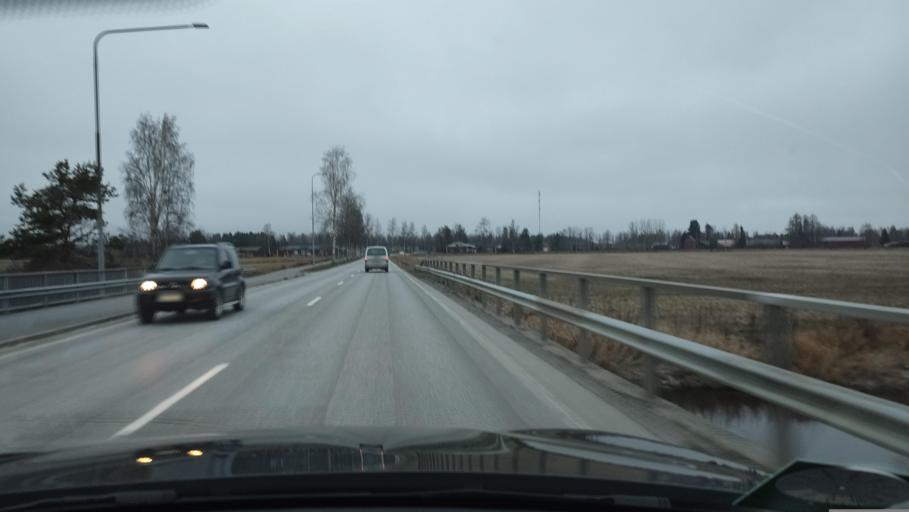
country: FI
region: Southern Ostrobothnia
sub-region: Suupohja
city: Kauhajoki
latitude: 62.4498
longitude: 22.2031
